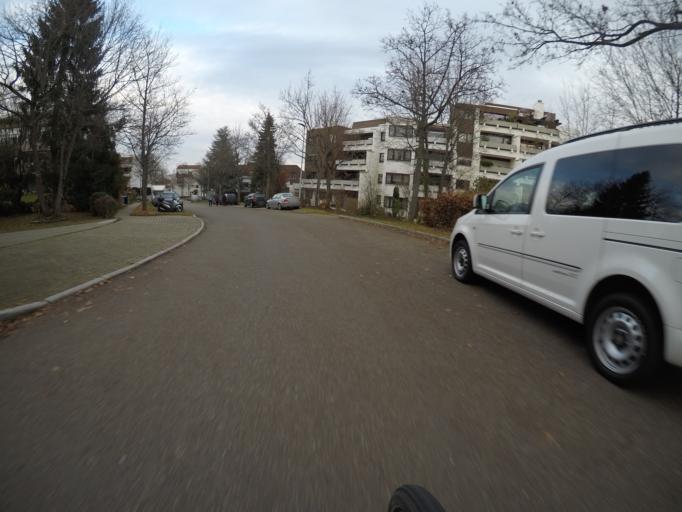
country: DE
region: Baden-Wuerttemberg
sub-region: Regierungsbezirk Stuttgart
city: Leinfelden-Echterdingen
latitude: 48.7001
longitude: 9.1347
